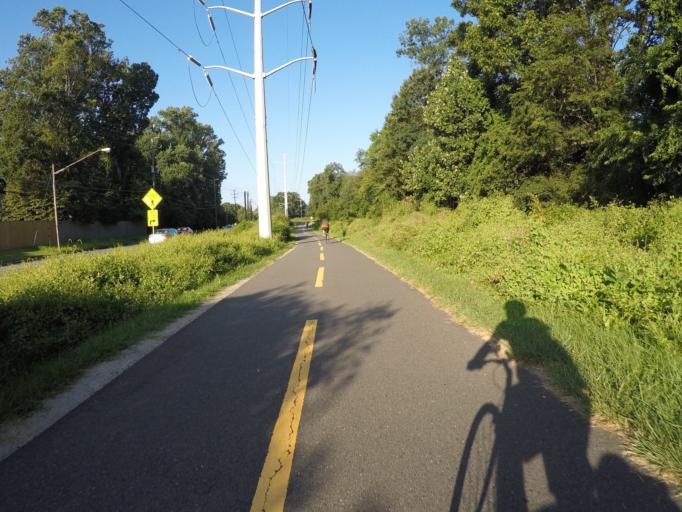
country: US
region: Virginia
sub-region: Fairfax County
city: Idylwood
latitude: 38.8906
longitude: -77.2039
